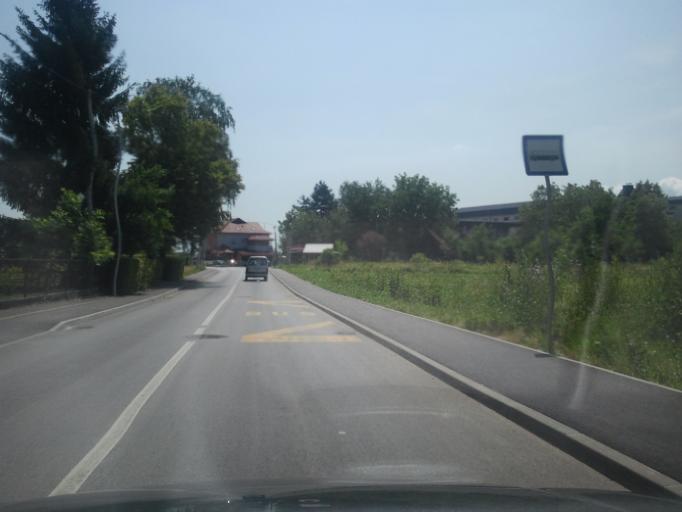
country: HR
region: Karlovacka
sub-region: Grad Karlovac
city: Karlovac
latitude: 45.4724
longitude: 15.5498
